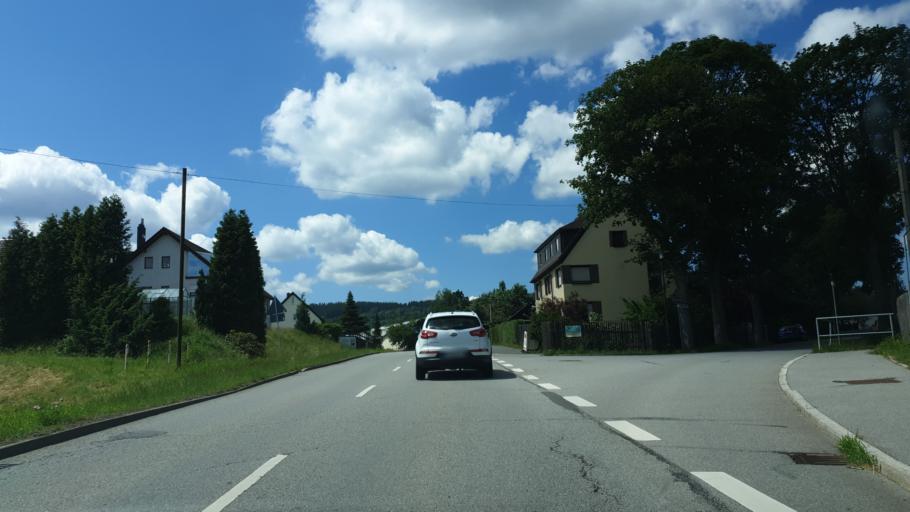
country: DE
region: Saxony
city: Schwarzenberg
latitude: 50.5365
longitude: 12.7752
